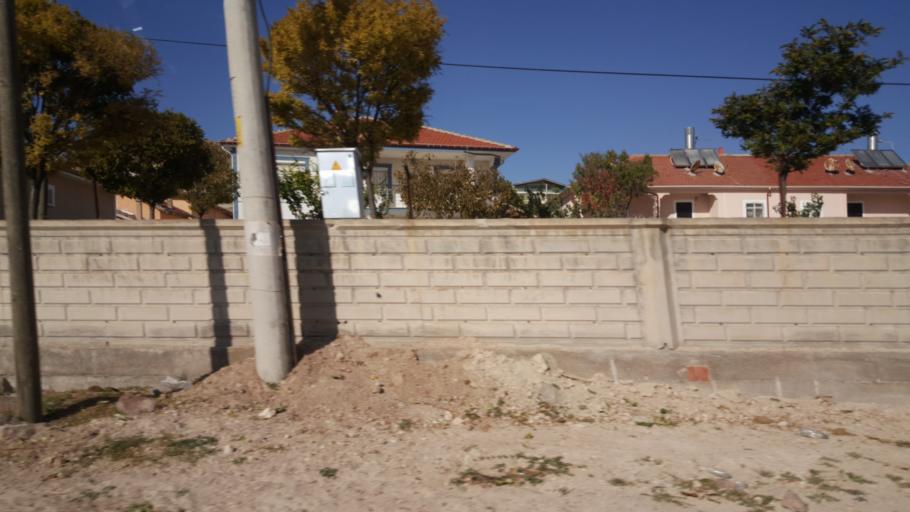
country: TR
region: Ankara
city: Altpinar
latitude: 39.1708
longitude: 32.6913
